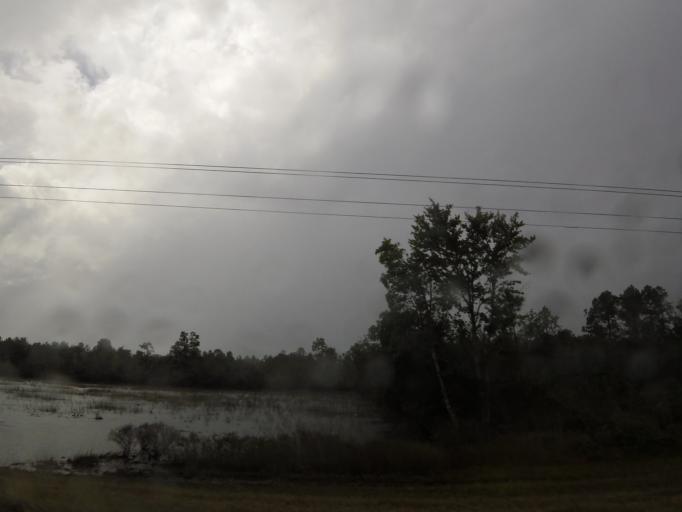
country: US
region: Florida
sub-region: Baker County
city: Macclenny
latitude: 30.3857
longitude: -82.1303
